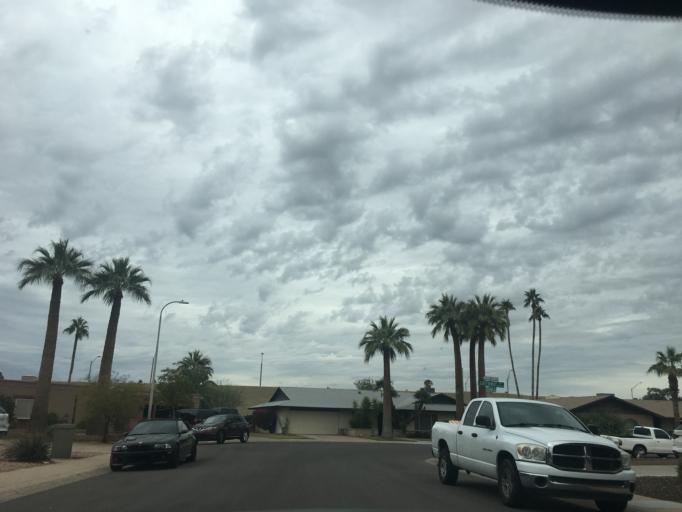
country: US
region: Arizona
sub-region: Maricopa County
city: Tempe
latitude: 33.3845
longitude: -111.9064
